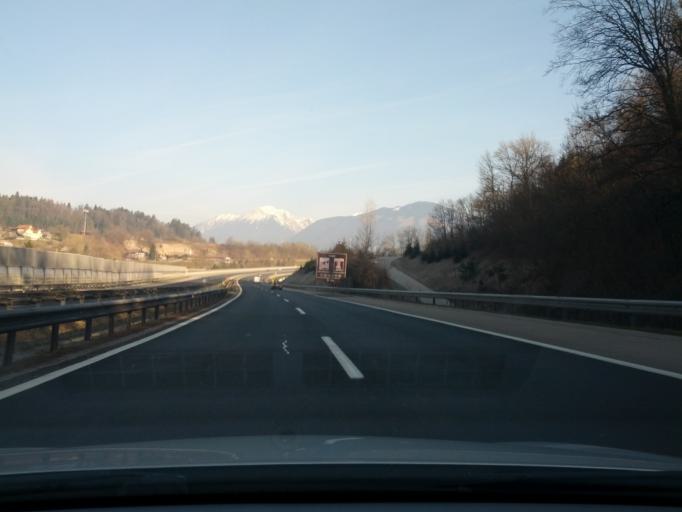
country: SI
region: Naklo
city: Naklo
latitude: 46.2887
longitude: 14.2876
